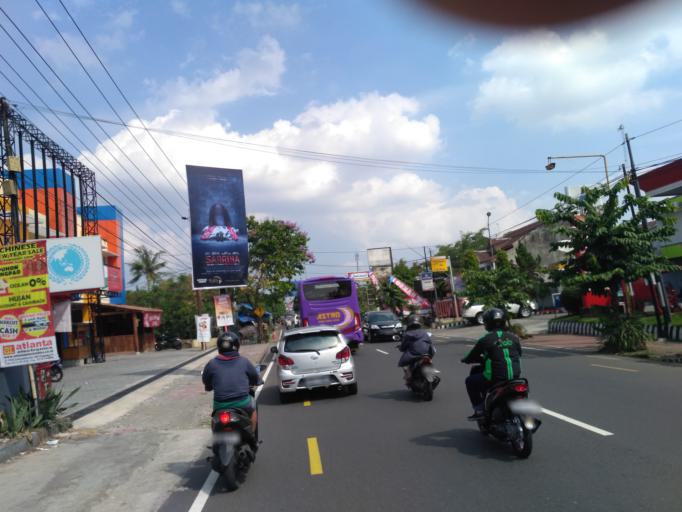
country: ID
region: Daerah Istimewa Yogyakarta
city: Yogyakarta
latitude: -7.7600
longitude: 110.3695
